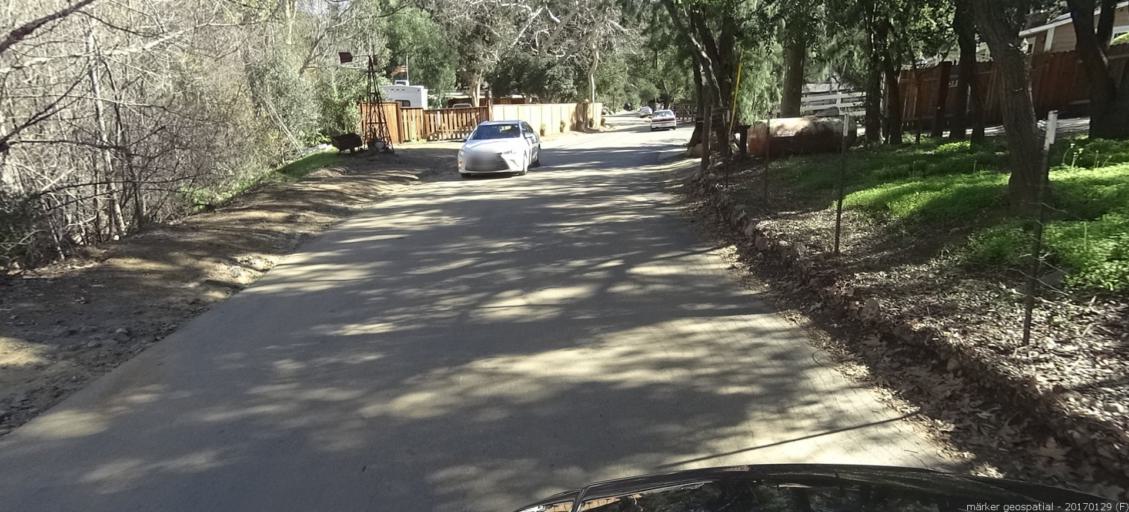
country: US
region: California
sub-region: Orange County
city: Portola Hills
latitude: 33.7082
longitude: -117.6323
